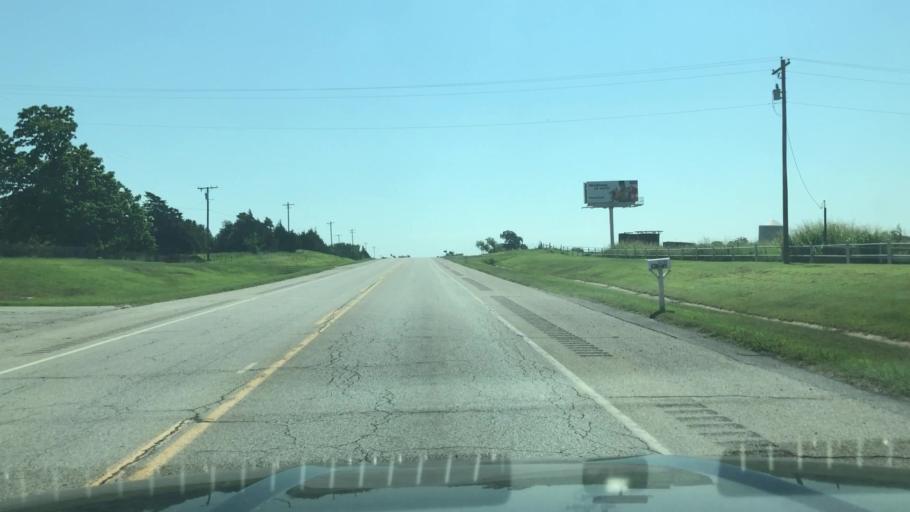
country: US
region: Oklahoma
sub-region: Creek County
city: Drumright
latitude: 35.9884
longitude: -96.5643
